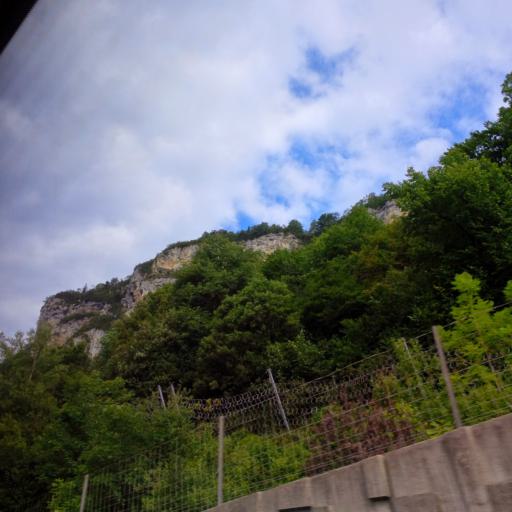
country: FR
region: Rhone-Alpes
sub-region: Departement de l'Ain
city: Nantua
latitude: 46.1623
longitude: 5.6587
